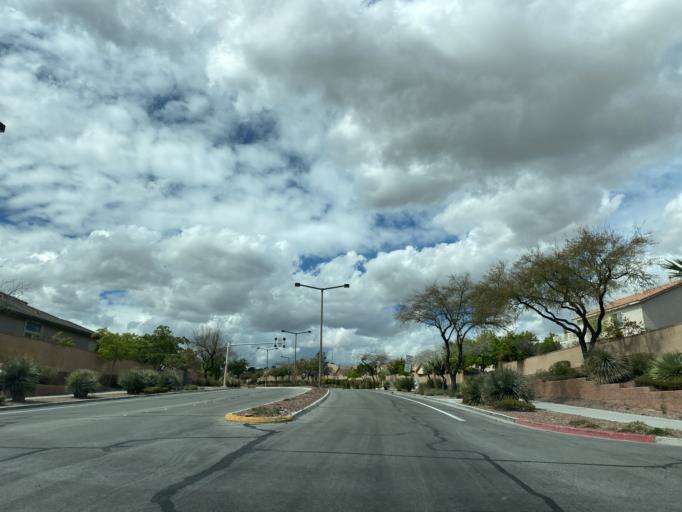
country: US
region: Nevada
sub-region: Clark County
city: Summerlin South
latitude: 36.1891
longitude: -115.3359
